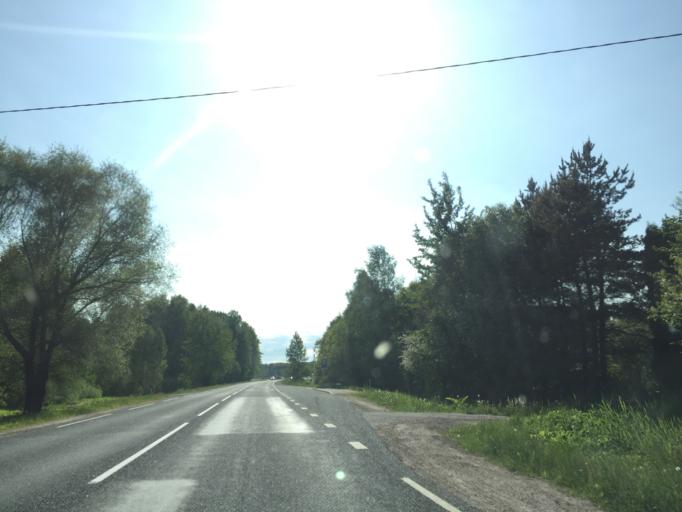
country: LV
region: Kekava
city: Kekava
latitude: 56.8149
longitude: 24.2796
